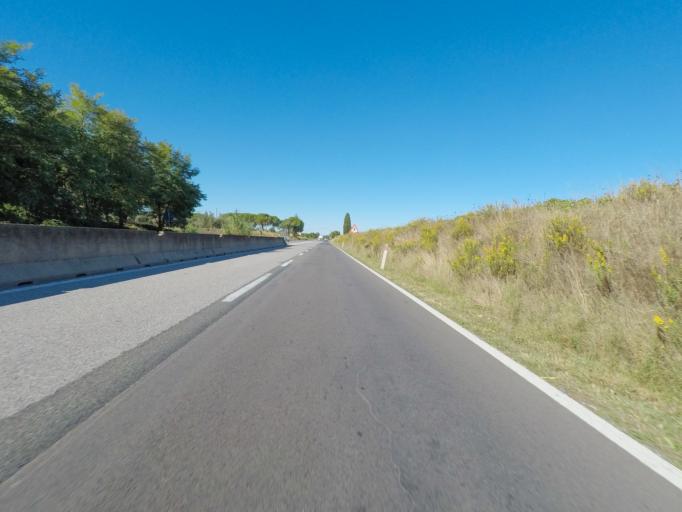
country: IT
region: Tuscany
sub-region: Provincia di Grosseto
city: Grosseto
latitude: 42.6877
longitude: 11.1389
